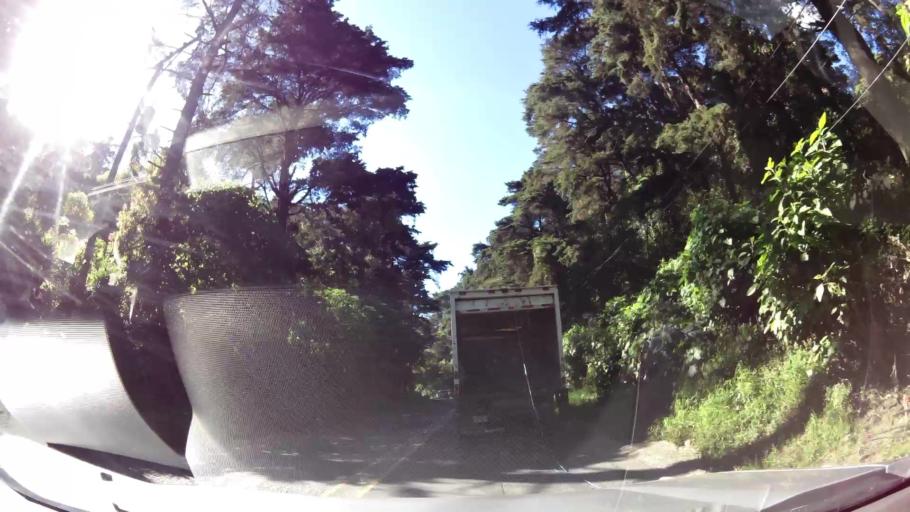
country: GT
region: Sacatepequez
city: Santa Lucia Milpas Altas
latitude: 14.5827
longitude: -90.6598
